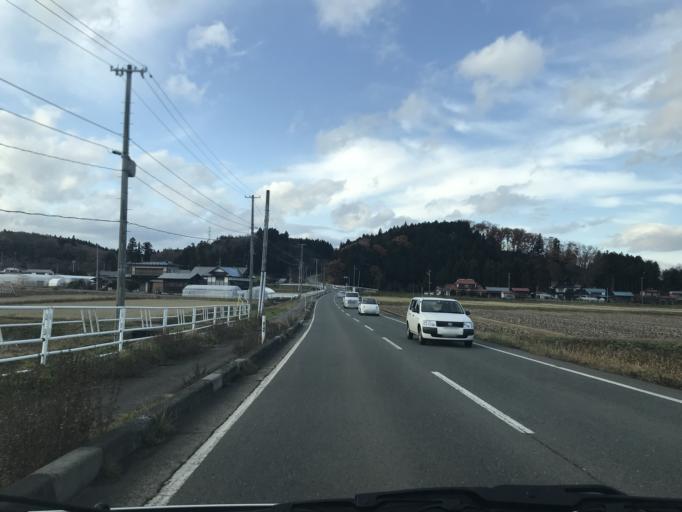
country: JP
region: Iwate
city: Mizusawa
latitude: 39.1674
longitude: 141.0886
